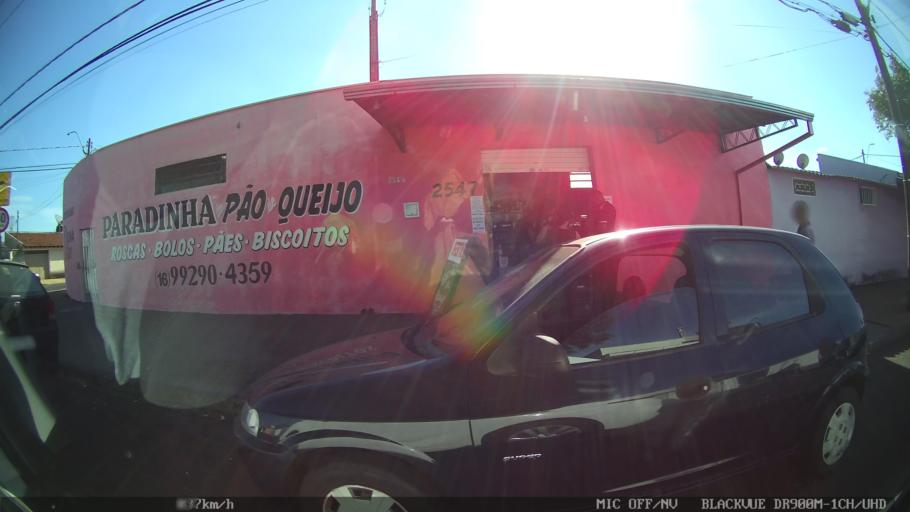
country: BR
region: Sao Paulo
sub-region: Franca
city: Franca
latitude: -20.4969
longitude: -47.4153
